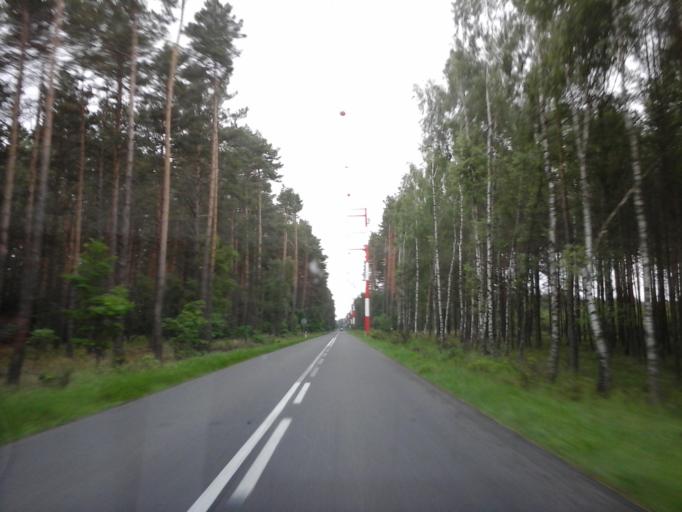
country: PL
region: West Pomeranian Voivodeship
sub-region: Powiat walecki
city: Miroslawiec
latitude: 53.3708
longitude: 16.1268
